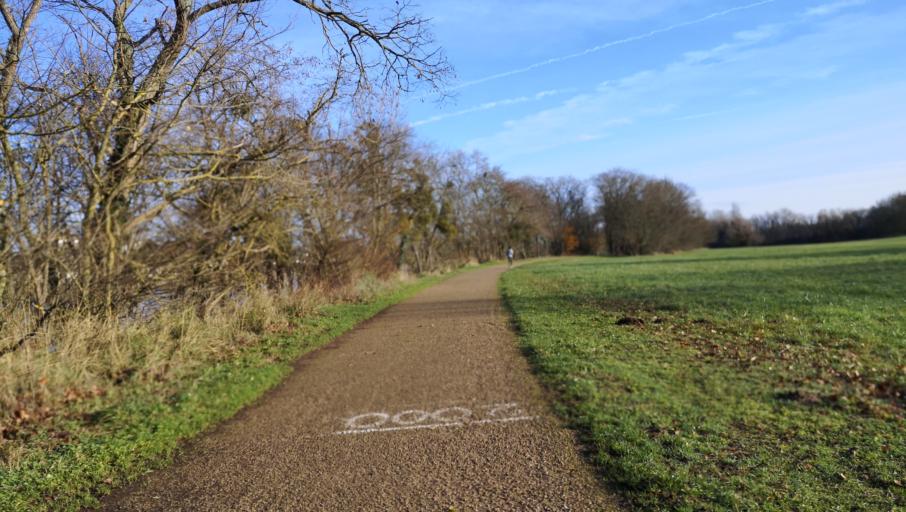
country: FR
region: Centre
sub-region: Departement du Loiret
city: Saint-Jean-le-Blanc
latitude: 47.8966
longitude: 1.9290
